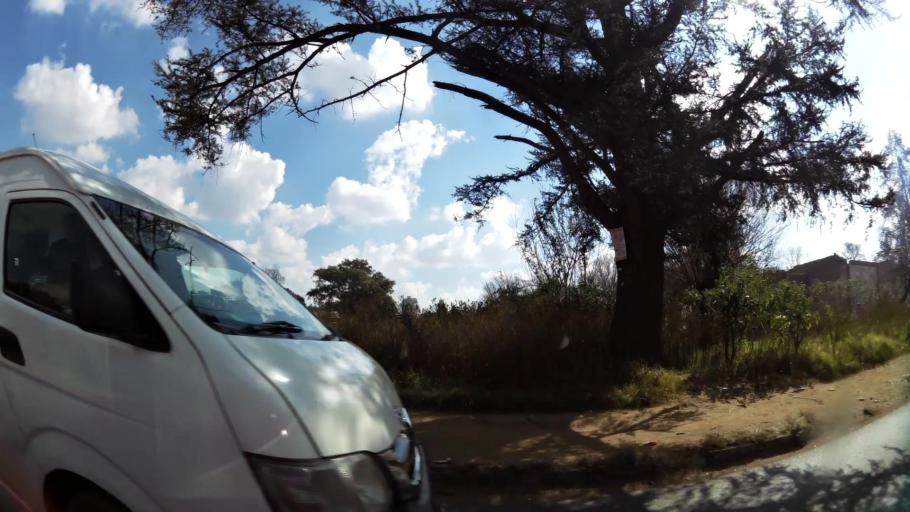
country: ZA
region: Gauteng
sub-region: City of Johannesburg Metropolitan Municipality
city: Roodepoort
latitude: -26.1755
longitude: 27.8726
